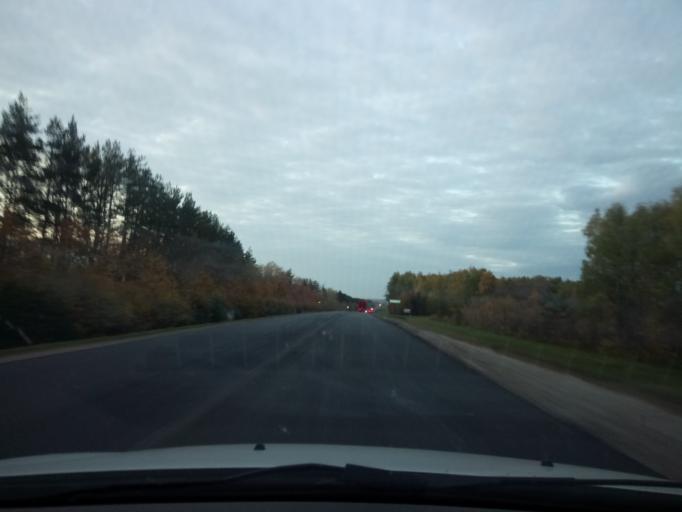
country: RU
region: Nizjnij Novgorod
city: Bol'shoye Murashkino
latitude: 55.8173
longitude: 44.7582
